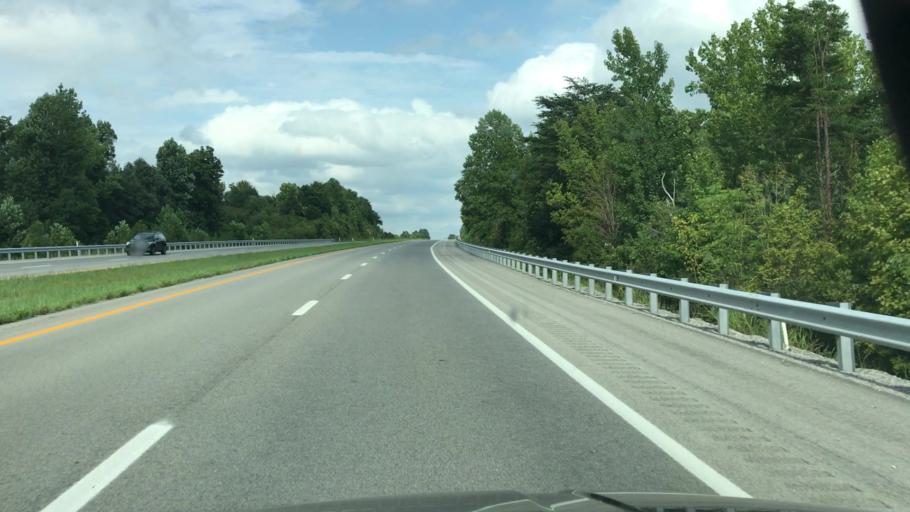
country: US
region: Kentucky
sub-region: Hopkins County
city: Dawson Springs
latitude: 37.1659
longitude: -87.7547
